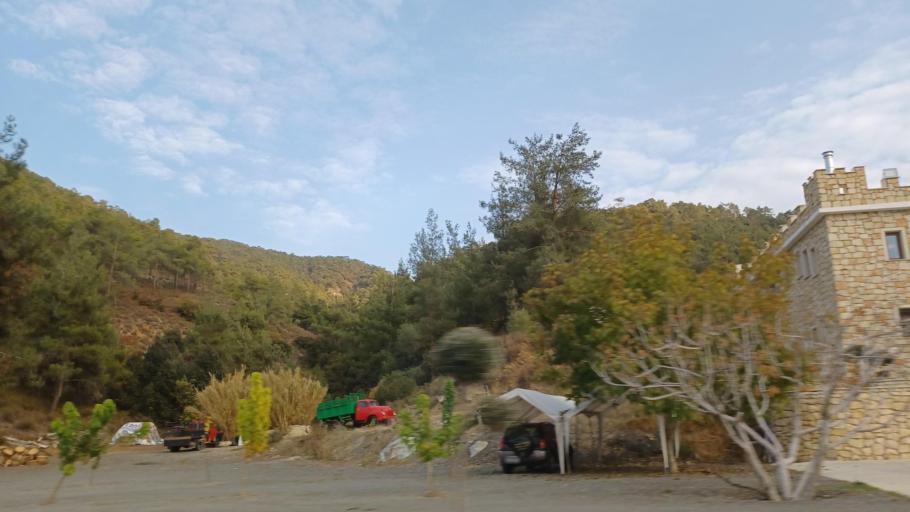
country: CY
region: Lefkosia
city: Kakopetria
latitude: 34.9714
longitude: 32.9195
